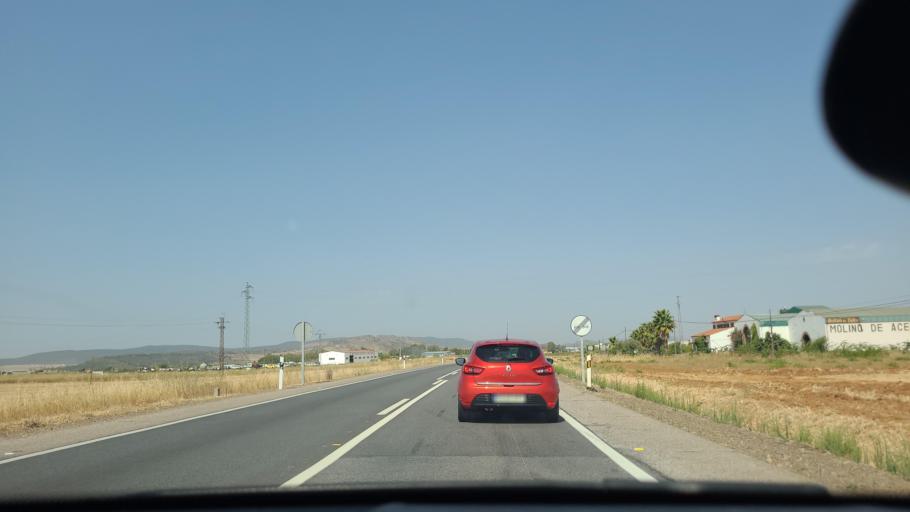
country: ES
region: Extremadura
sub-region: Provincia de Badajoz
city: Puebla de Sancho Perez
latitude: 38.4102
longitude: -6.3872
